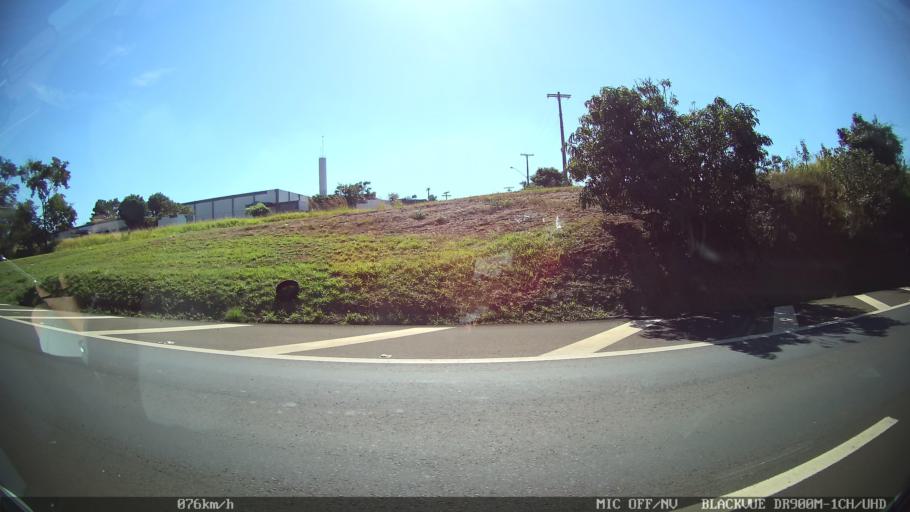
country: BR
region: Sao Paulo
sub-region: Franca
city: Franca
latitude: -20.5576
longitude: -47.4412
